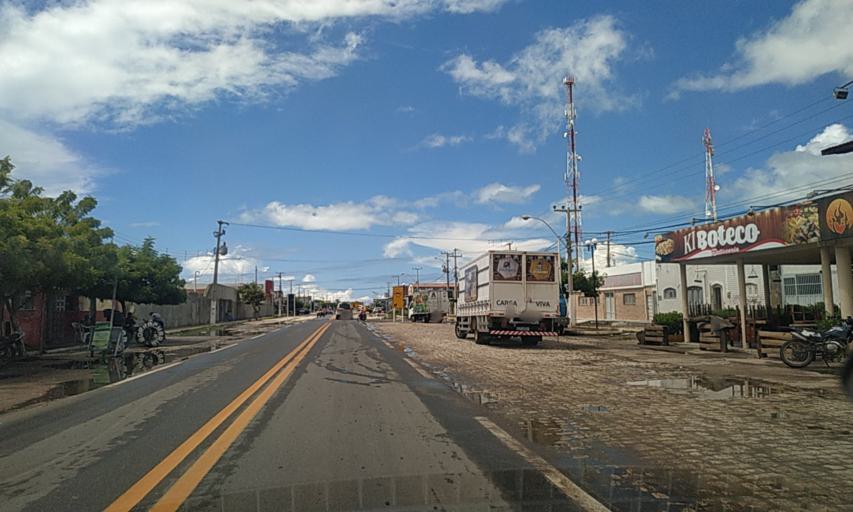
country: BR
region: Rio Grande do Norte
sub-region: Areia Branca
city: Areia Branca
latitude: -4.9534
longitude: -37.1287
